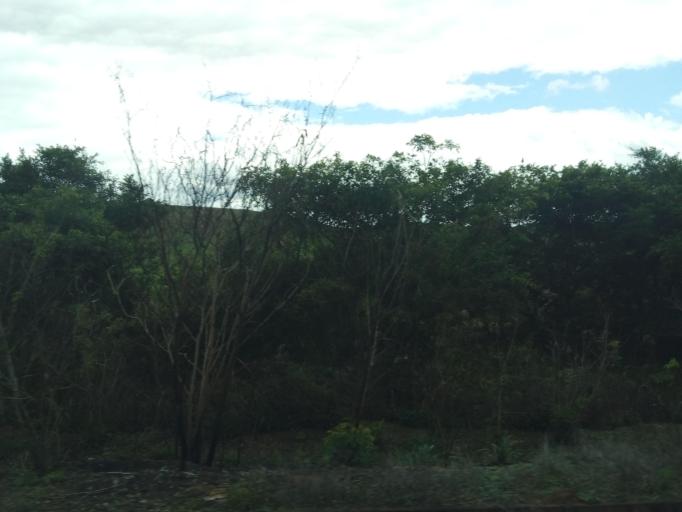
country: BR
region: Minas Gerais
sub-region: Governador Valadares
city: Governador Valadares
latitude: -19.0631
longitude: -42.1491
